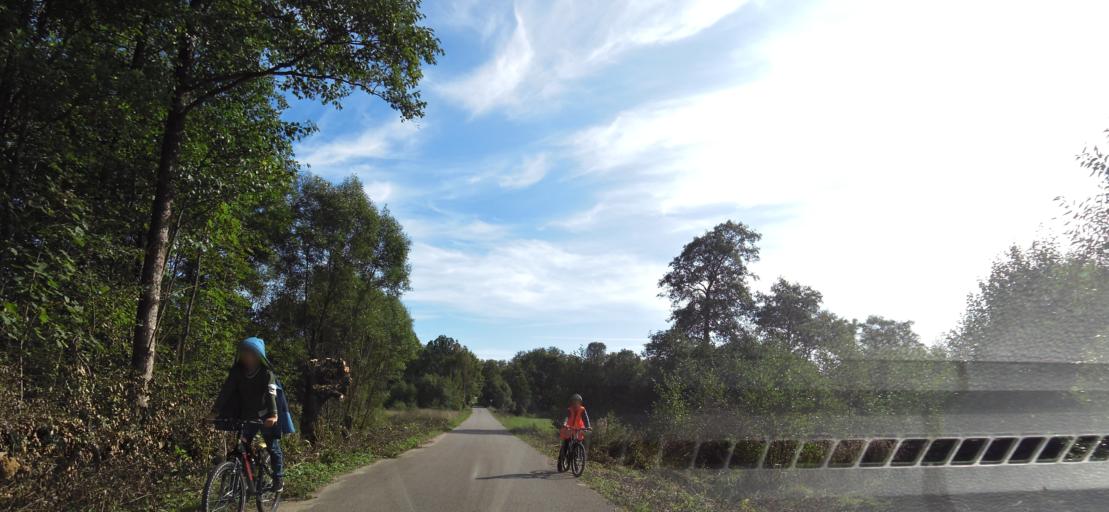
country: LT
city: Salcininkai
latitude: 54.4491
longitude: 25.5165
